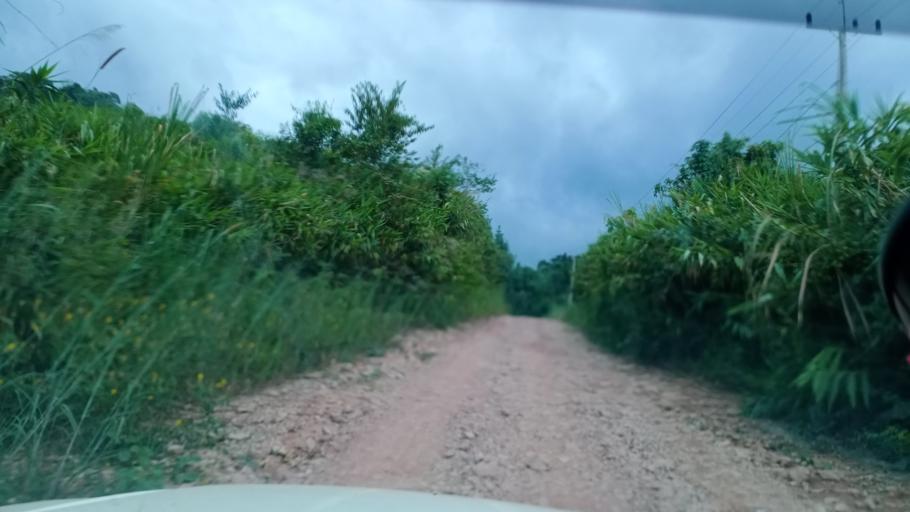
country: TH
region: Changwat Bueng Kan
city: Pak Khat
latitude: 18.7257
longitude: 103.2641
